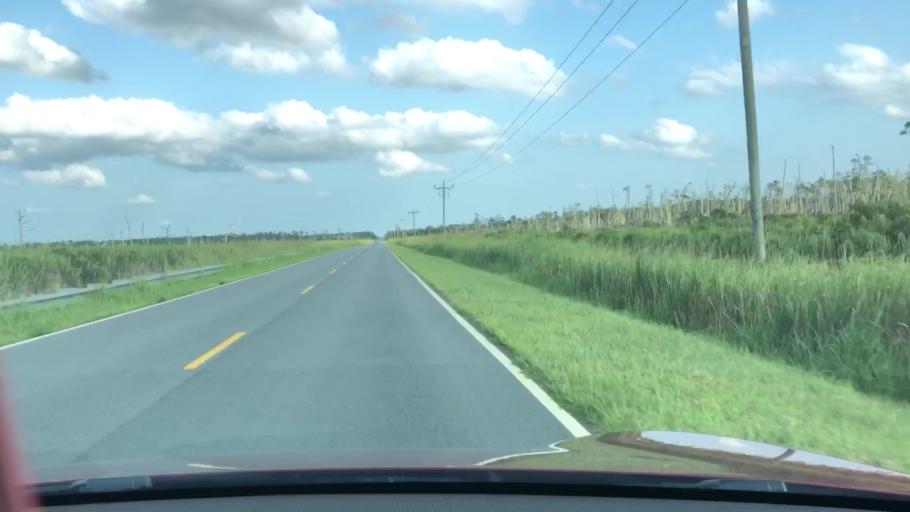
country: US
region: North Carolina
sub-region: Dare County
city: Wanchese
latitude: 35.6284
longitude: -75.8504
